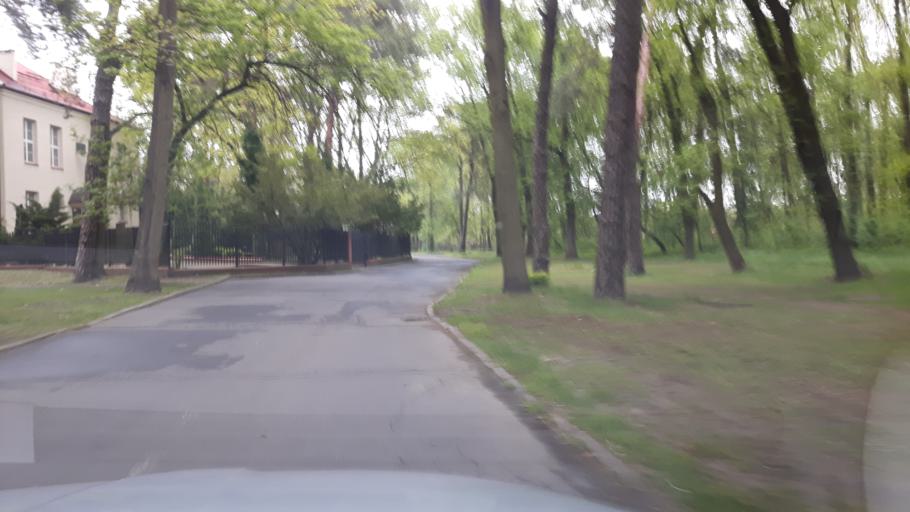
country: PL
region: Masovian Voivodeship
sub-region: Warszawa
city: Rembertow
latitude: 52.2652
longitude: 21.1787
